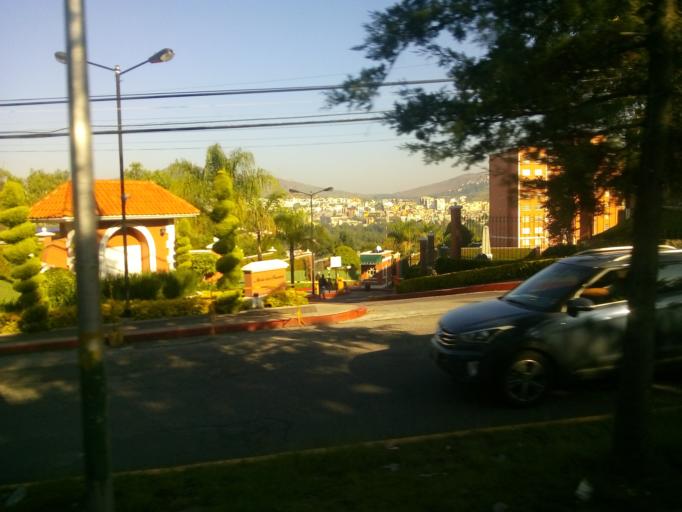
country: MX
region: Mexico
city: Vista Hermosa
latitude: 19.5185
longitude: -99.2474
